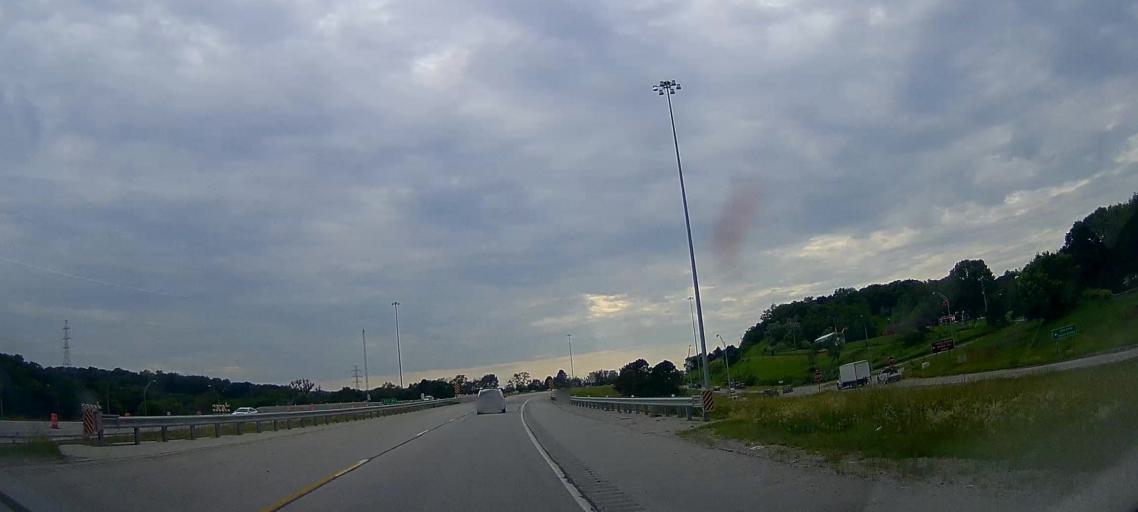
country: US
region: Iowa
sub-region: Pottawattamie County
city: Carter Lake
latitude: 41.3449
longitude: -95.9632
